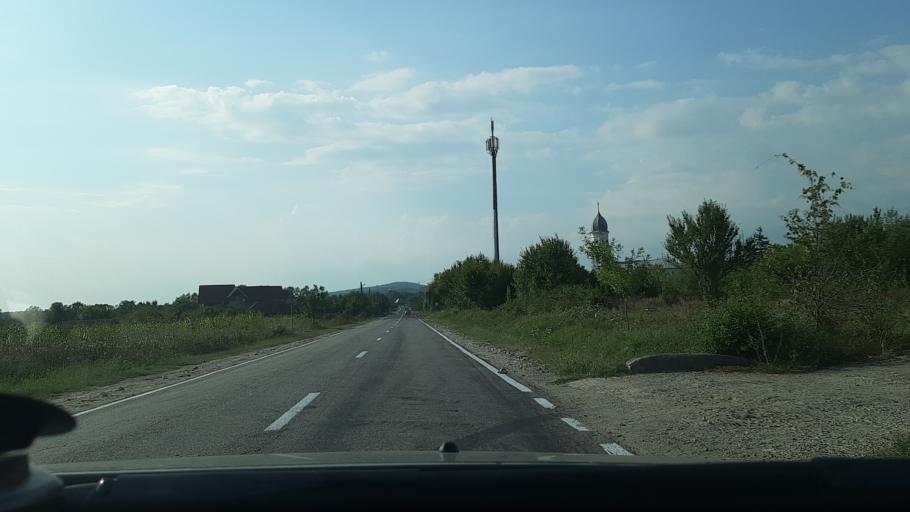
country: RO
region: Gorj
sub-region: Comuna Scoarta
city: Scoarta
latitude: 45.0150
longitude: 23.4699
